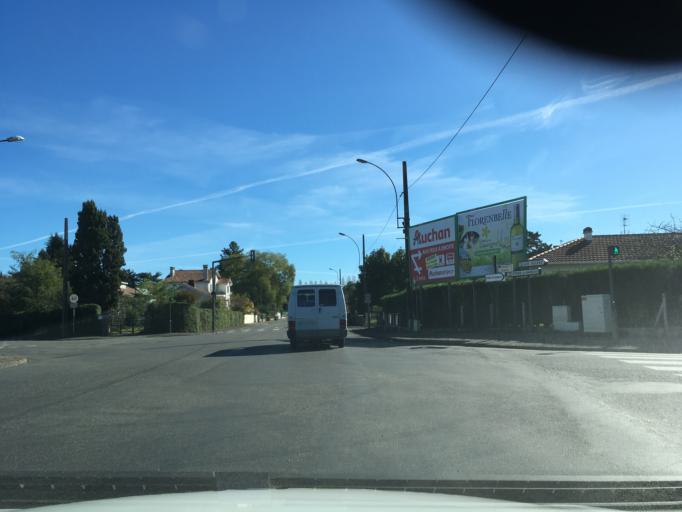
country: FR
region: Aquitaine
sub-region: Departement des Pyrenees-Atlantiques
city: Idron
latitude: 43.3124
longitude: -0.3273
